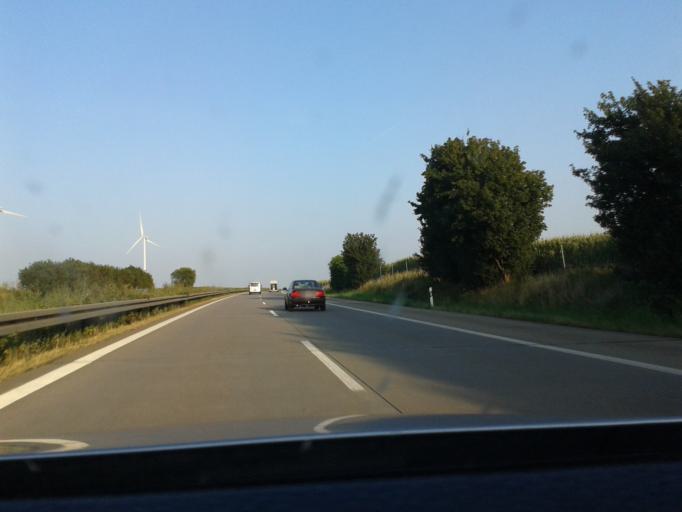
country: DE
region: Saxony
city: Nerchau
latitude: 51.2518
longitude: 12.8369
